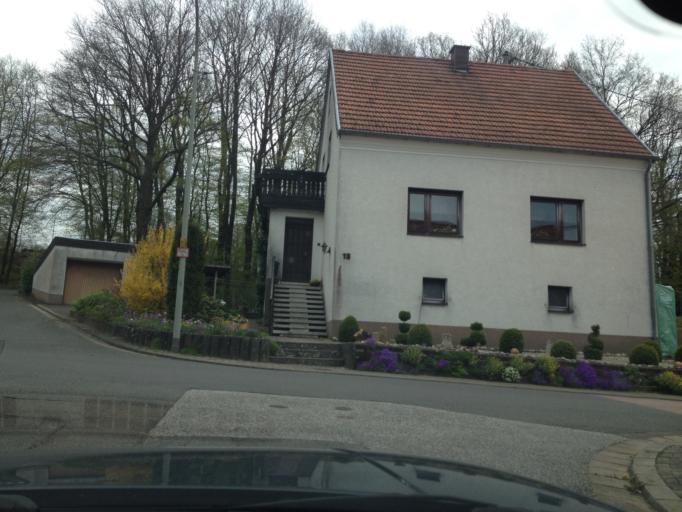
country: DE
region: Saarland
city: Namborn
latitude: 49.5141
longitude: 7.1797
